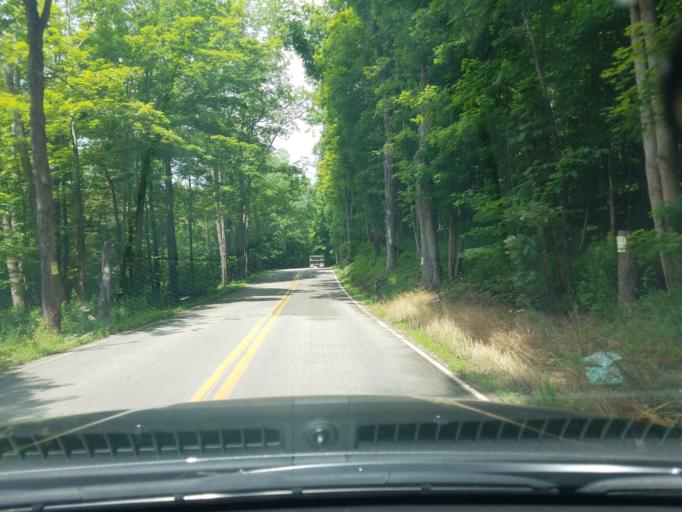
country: US
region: Pennsylvania
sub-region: Fayette County
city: Bear Rocks
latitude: 40.1631
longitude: -79.3535
